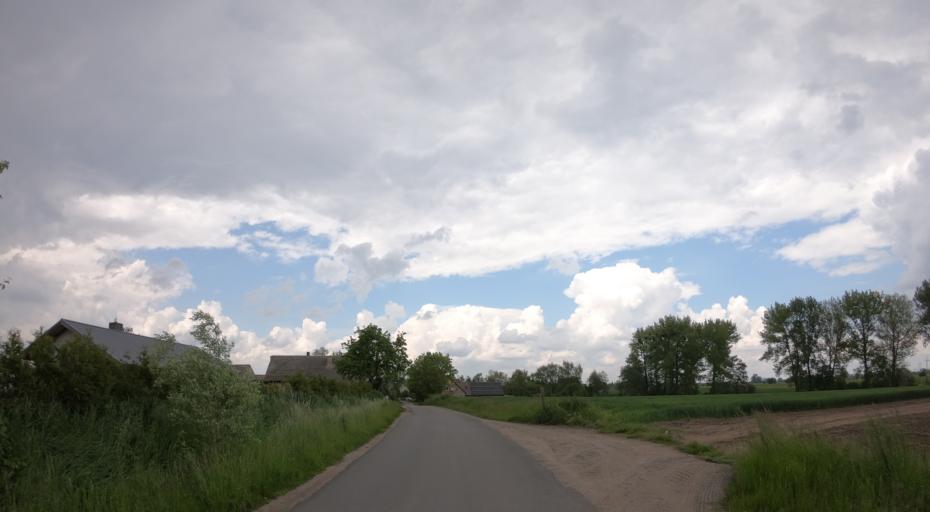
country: PL
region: West Pomeranian Voivodeship
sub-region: Powiat pyrzycki
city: Bielice
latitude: 53.2247
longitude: 14.7676
